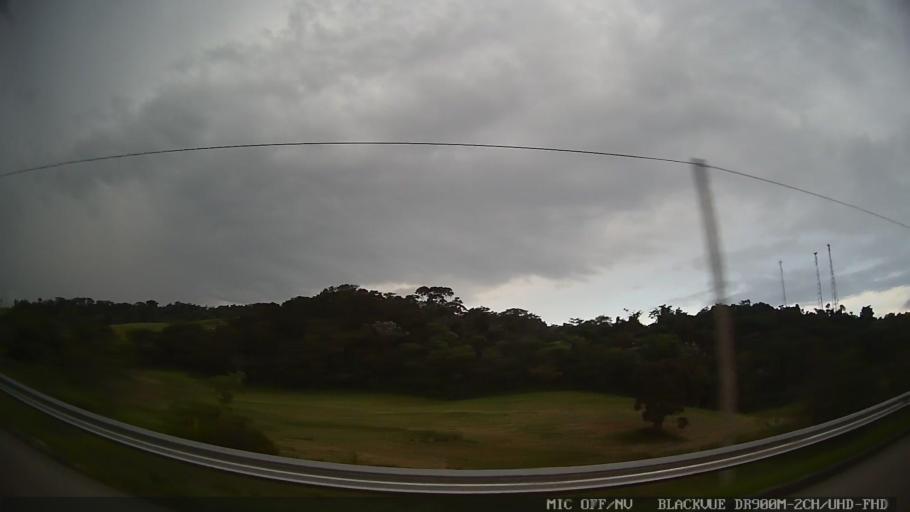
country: BR
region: Sao Paulo
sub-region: Santa Branca
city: Santa Branca
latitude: -23.4322
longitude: -45.6242
